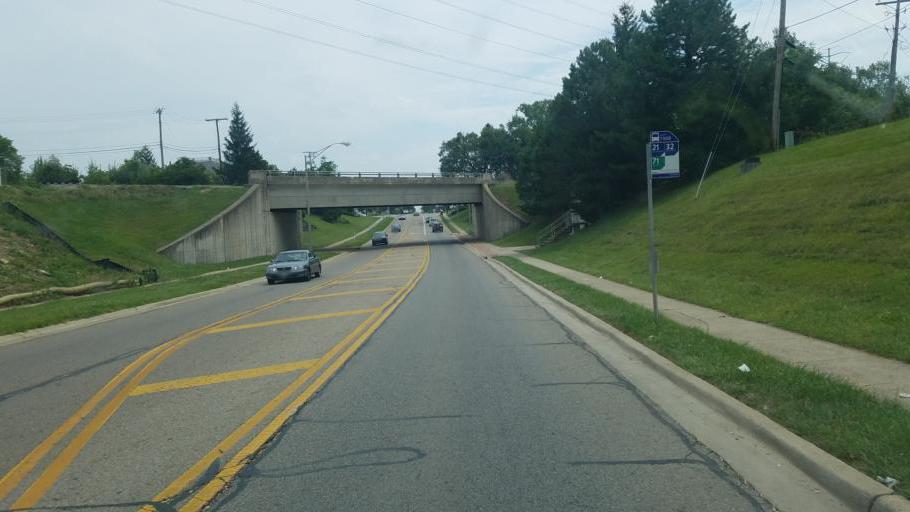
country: US
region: Ohio
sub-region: Franklin County
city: Hilliard
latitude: 40.0302
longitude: -83.1557
